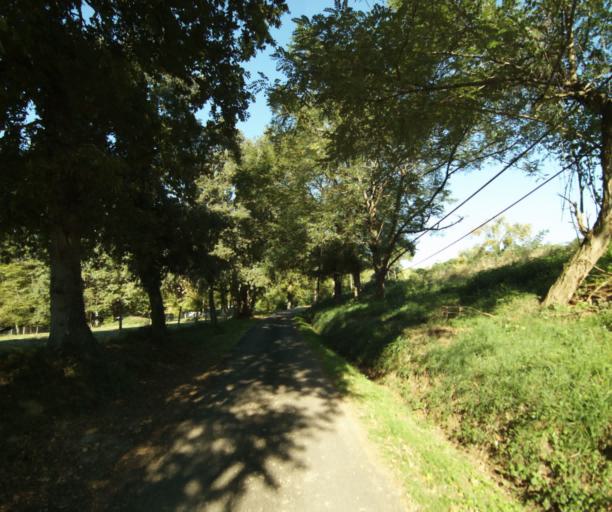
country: FR
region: Midi-Pyrenees
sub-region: Departement du Gers
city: Cazaubon
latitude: 43.9549
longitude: -0.0362
